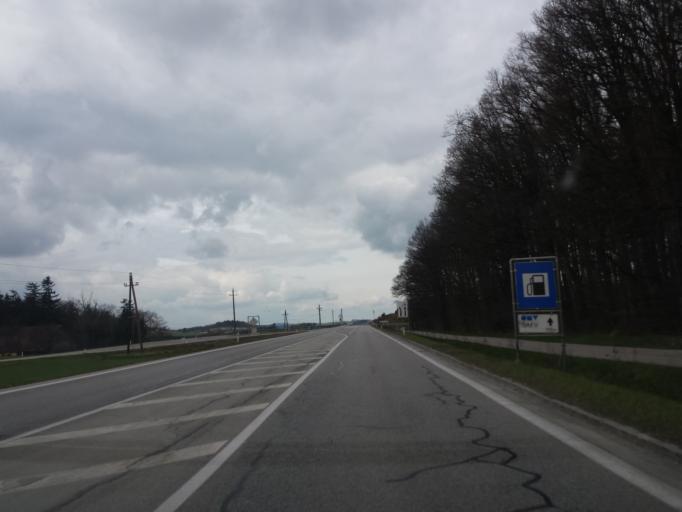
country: AT
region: Lower Austria
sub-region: Politischer Bezirk Krems
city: Gfohl
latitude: 48.5037
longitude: 15.5264
